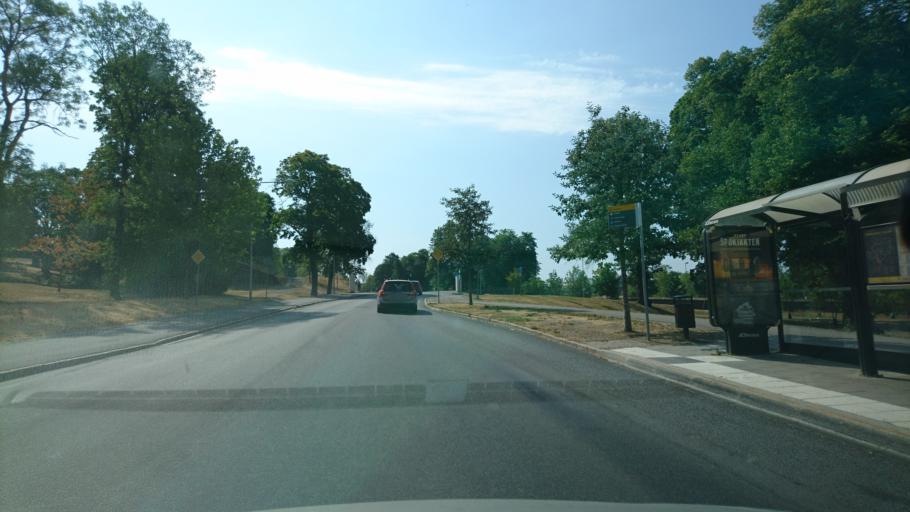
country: SE
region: Uppsala
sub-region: Uppsala Kommun
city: Uppsala
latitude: 59.8547
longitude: 17.6323
